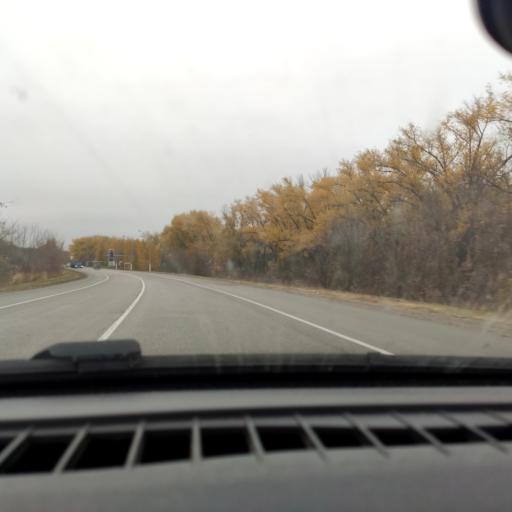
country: RU
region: Voronezj
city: Devitsa
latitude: 51.5946
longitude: 38.9775
